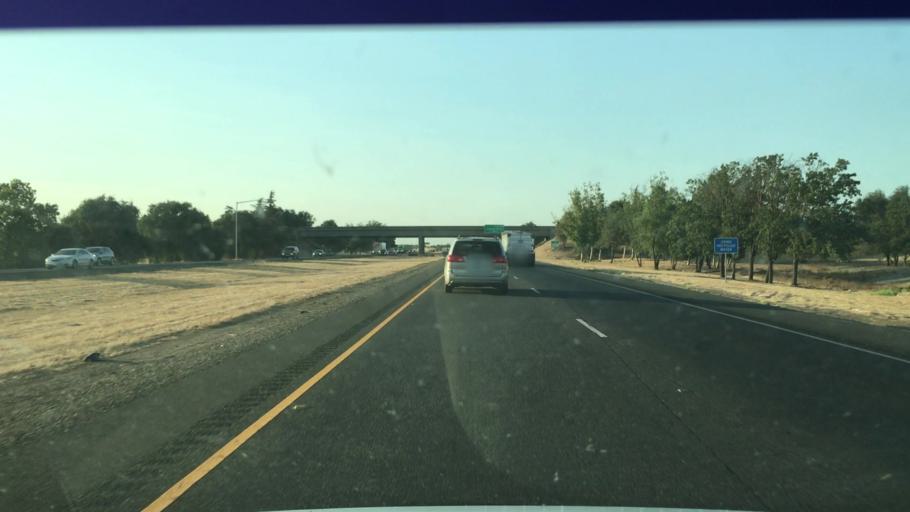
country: US
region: California
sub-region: Sacramento County
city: Laguna
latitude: 38.4066
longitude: -121.4832
